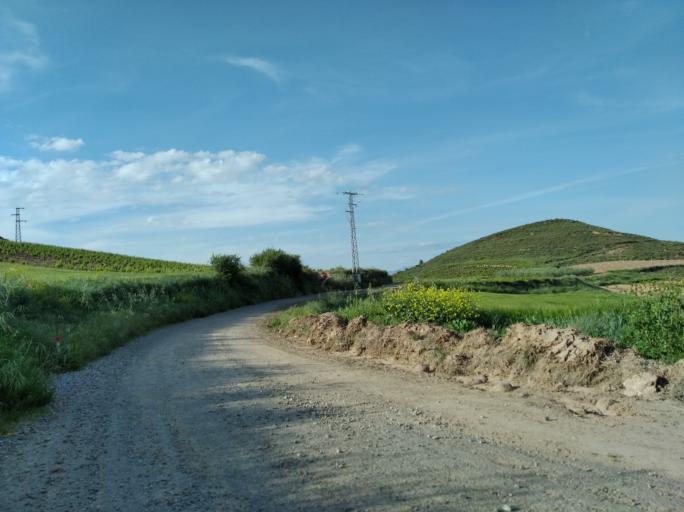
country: ES
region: La Rioja
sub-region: Provincia de La Rioja
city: Sojuela
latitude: 42.3720
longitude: -2.5448
